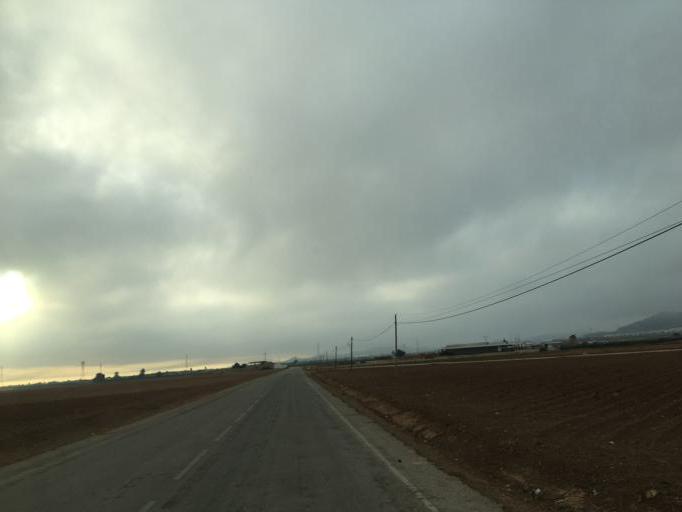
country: ES
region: Murcia
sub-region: Murcia
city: Cartagena
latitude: 37.6641
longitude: -0.9503
